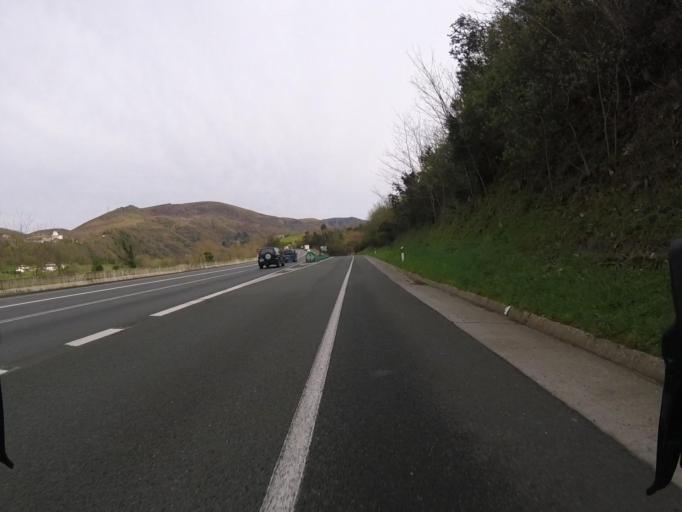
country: ES
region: Basque Country
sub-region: Provincia de Guipuzcoa
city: Irun
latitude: 43.3317
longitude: -1.7515
